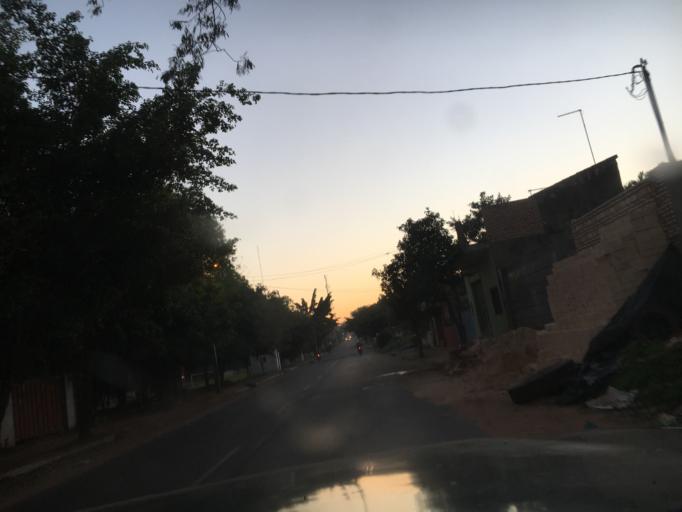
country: PY
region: Central
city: Villa Elisa
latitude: -25.3724
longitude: -57.5883
